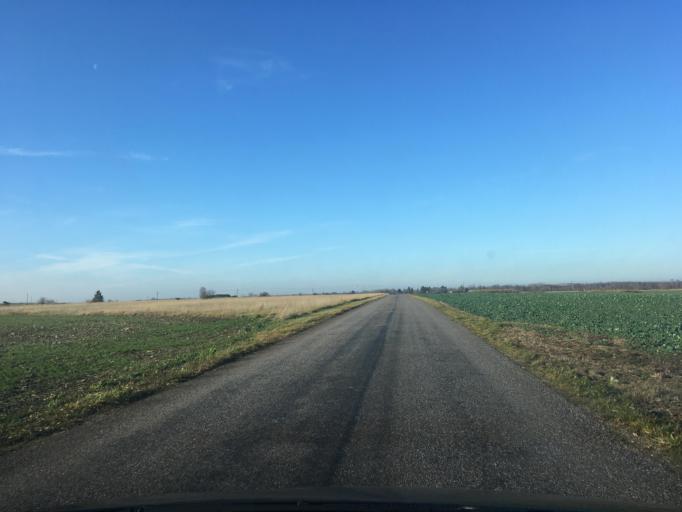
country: EE
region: Harju
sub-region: Maardu linn
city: Maardu
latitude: 59.4511
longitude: 25.1140
